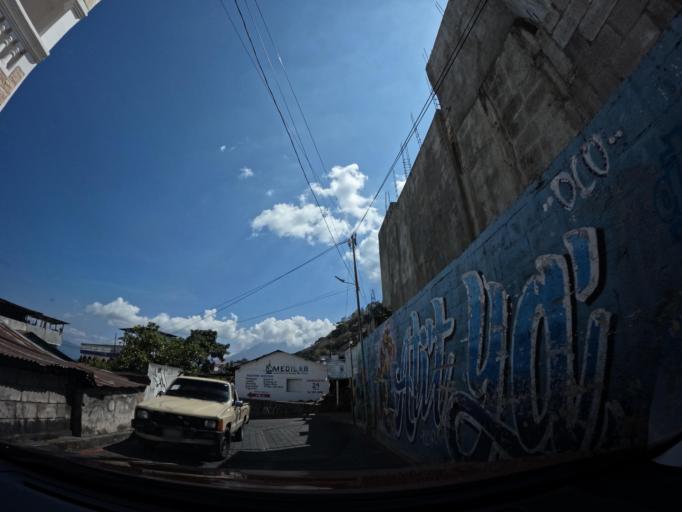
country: GT
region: Solola
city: San Pedro La Laguna
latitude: 14.6894
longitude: -91.2715
